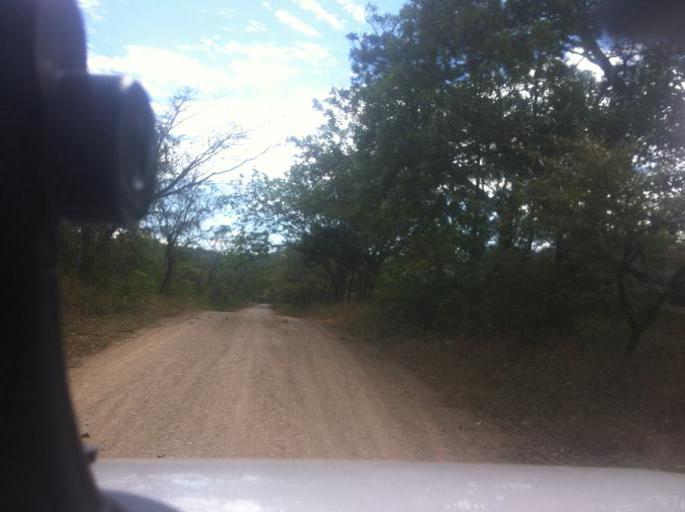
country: NI
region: Rivas
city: Belen
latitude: 11.5909
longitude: -86.0253
